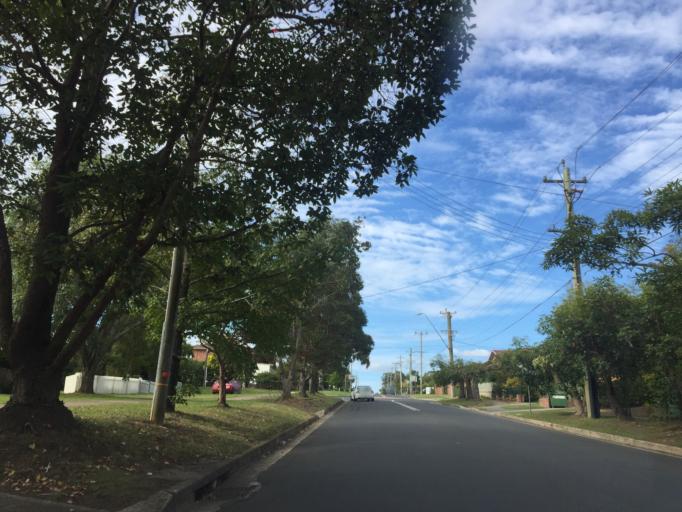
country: AU
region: New South Wales
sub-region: The Hills Shire
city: Beaumont Hills
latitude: -33.7133
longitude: 150.9609
